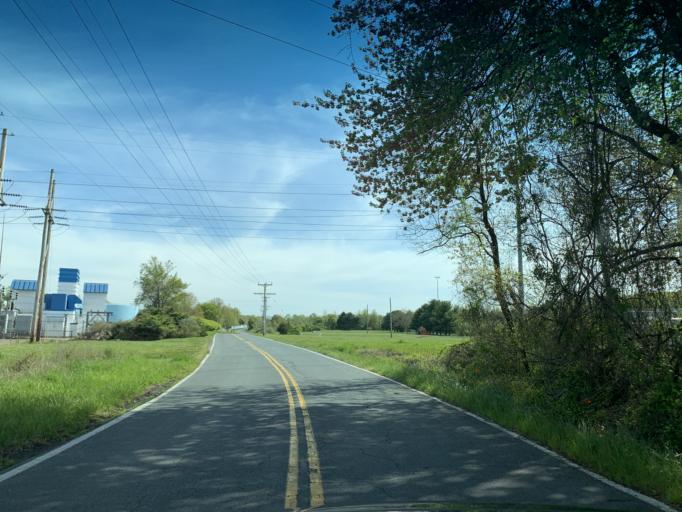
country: US
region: Maryland
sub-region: Harford County
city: Perryman
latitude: 39.4423
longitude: -76.2156
